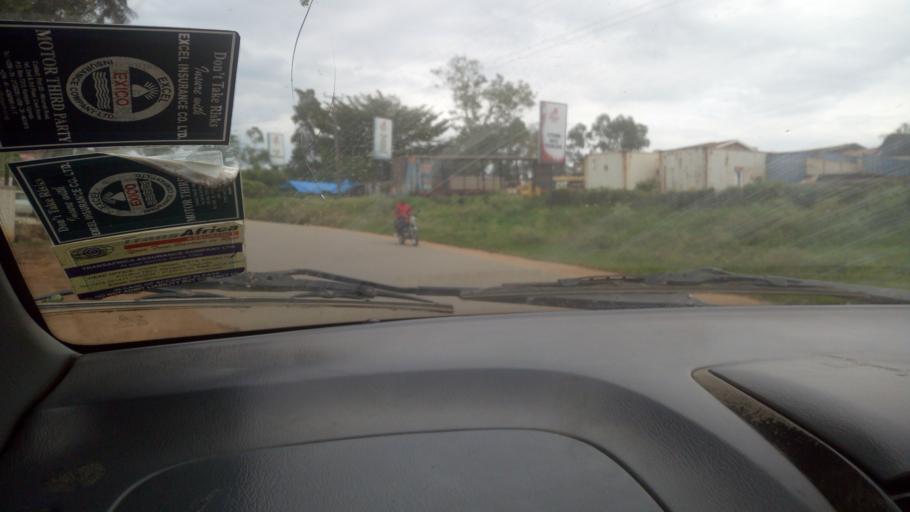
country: UG
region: Western Region
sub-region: Mbarara District
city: Mbarara
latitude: -0.6030
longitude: 30.6506
